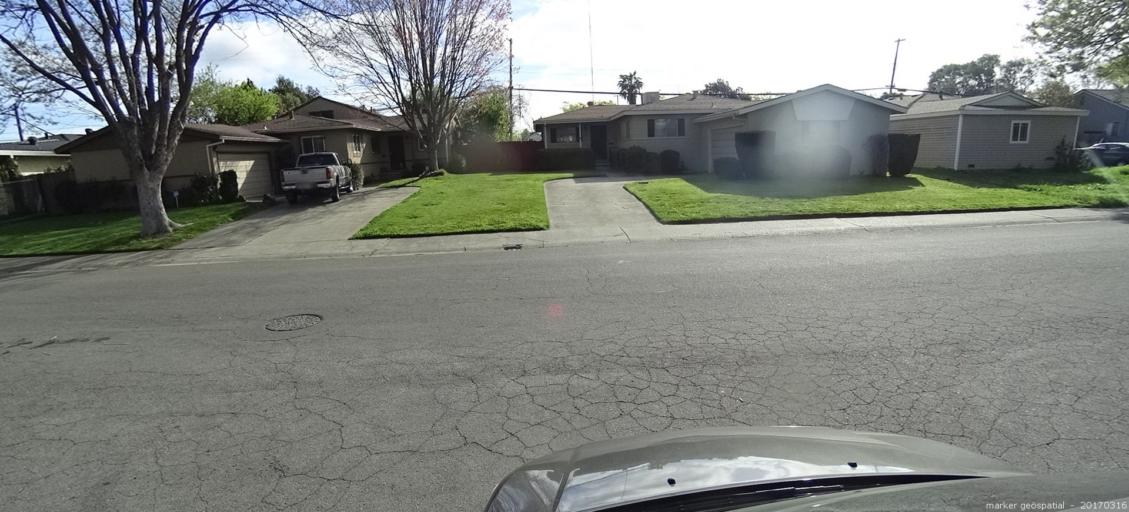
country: US
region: California
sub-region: Sacramento County
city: Parkway
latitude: 38.5052
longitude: -121.4837
